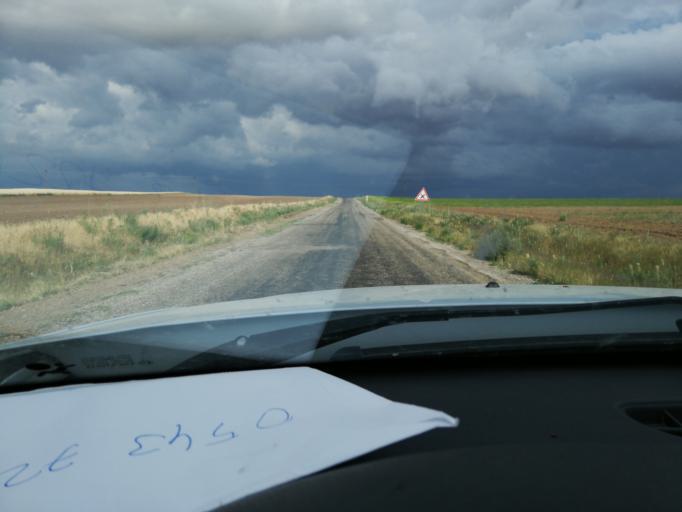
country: TR
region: Kirsehir
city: Kirsehir
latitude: 39.0414
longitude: 34.1727
